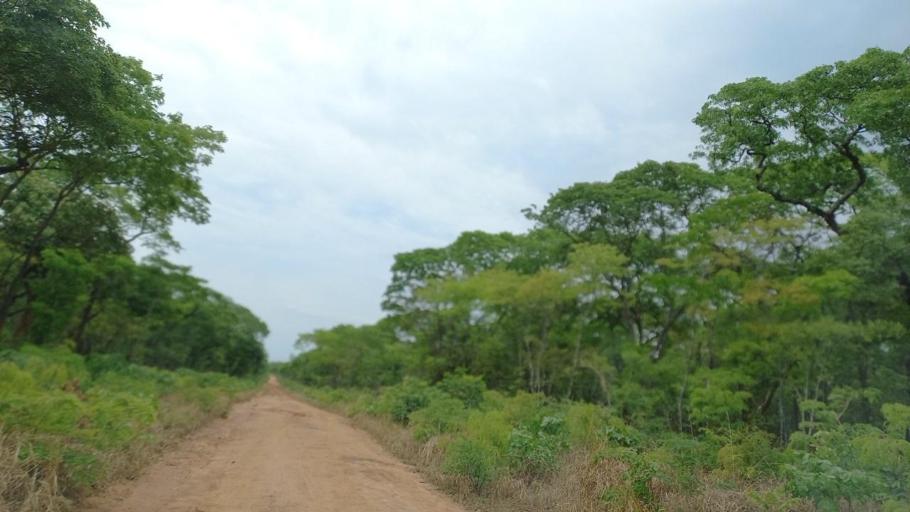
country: ZM
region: North-Western
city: Kalengwa
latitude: -13.5851
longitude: 24.9718
